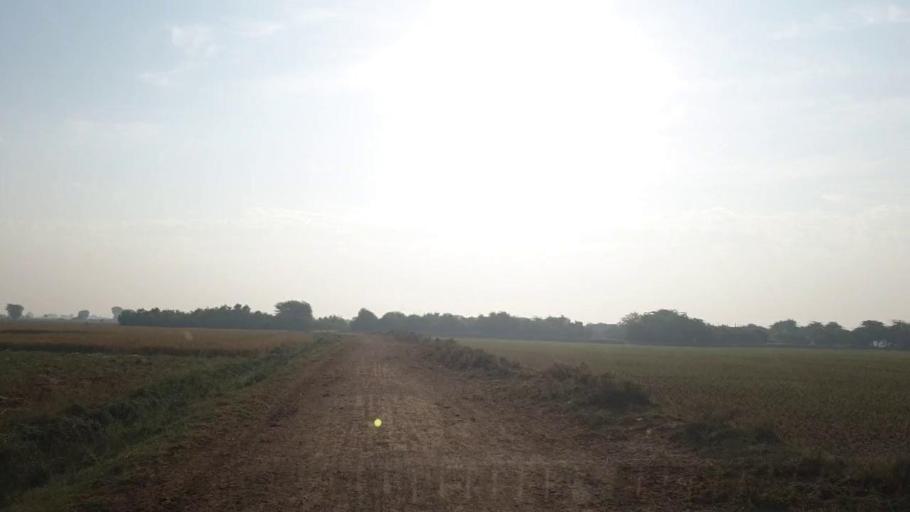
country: PK
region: Sindh
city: Tando Bago
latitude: 24.8212
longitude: 68.9596
